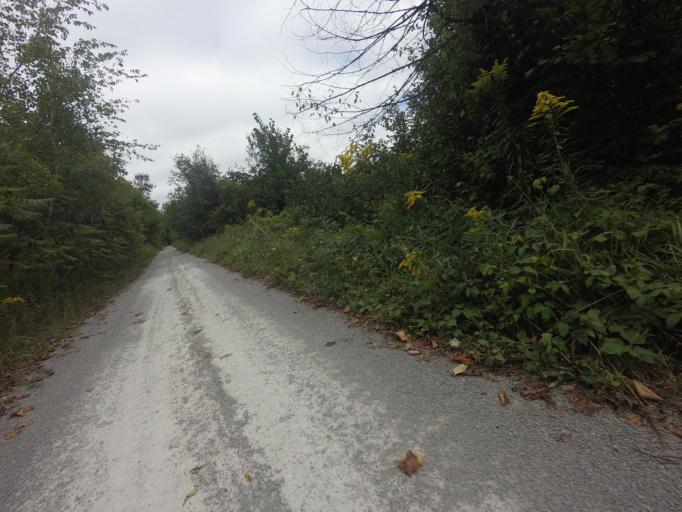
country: CA
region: Ontario
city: Uxbridge
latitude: 44.2592
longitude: -79.0284
